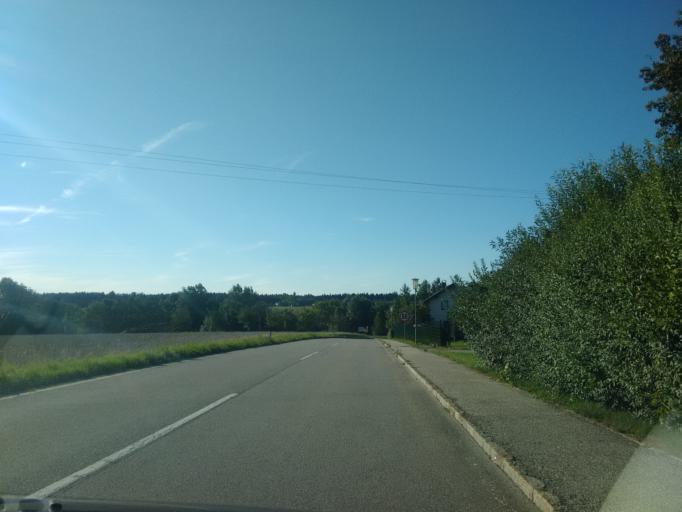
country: AT
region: Upper Austria
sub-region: Wels-Land
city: Thalheim bei Wels
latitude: 48.1199
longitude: 14.0925
